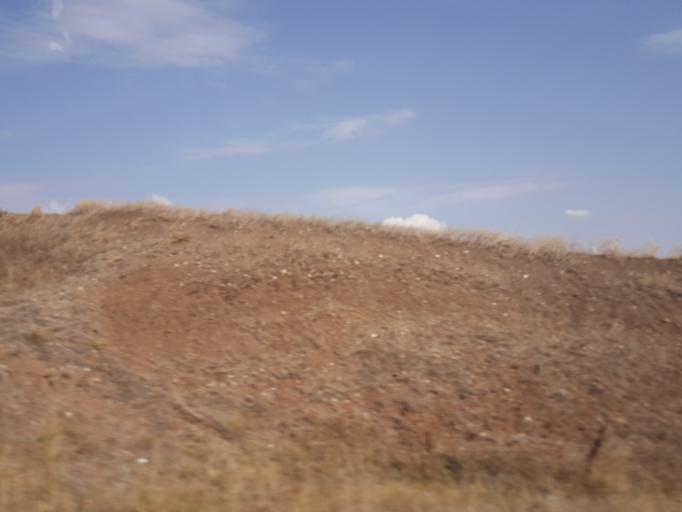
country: TR
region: Corum
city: Alaca
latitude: 40.1537
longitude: 34.8775
